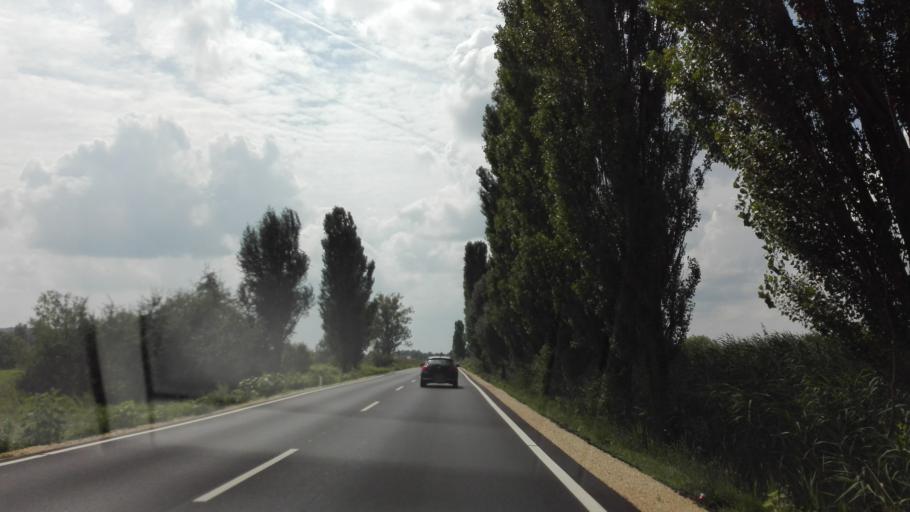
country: HU
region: Tolna
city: Simontornya
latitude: 46.7627
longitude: 18.5628
